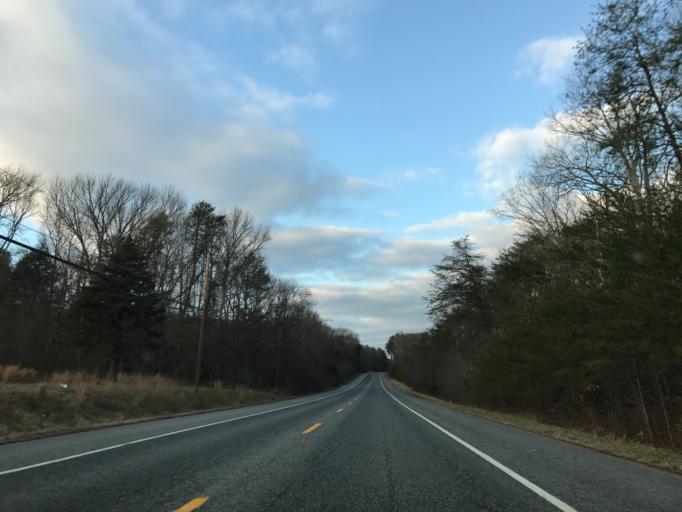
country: US
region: Maryland
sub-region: Cecil County
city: Charlestown
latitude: 39.5358
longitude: -75.9517
